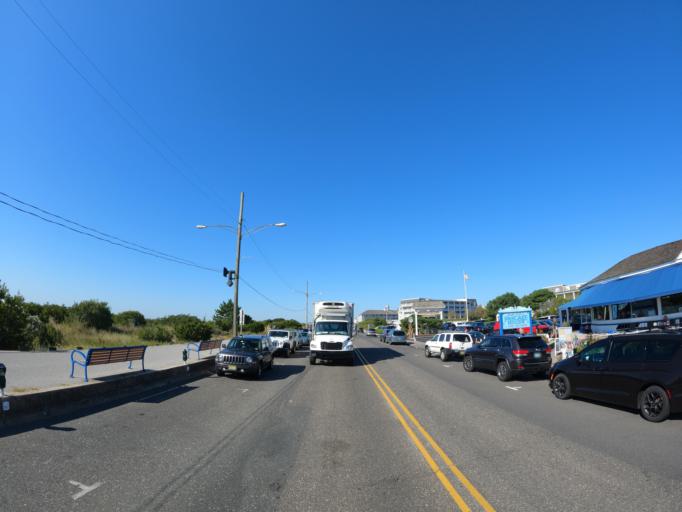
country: US
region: New Jersey
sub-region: Cape May County
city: Cape May
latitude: 38.9303
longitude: -74.9232
